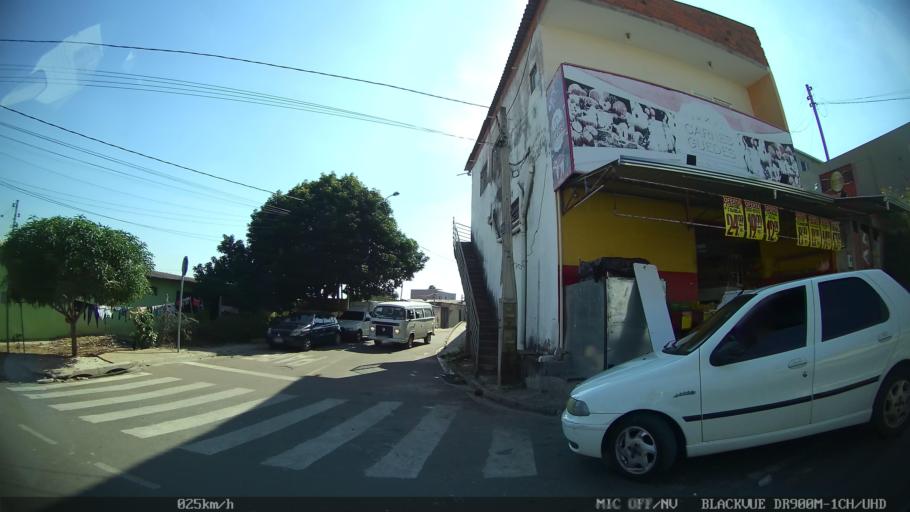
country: BR
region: Sao Paulo
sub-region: Campinas
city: Campinas
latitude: -22.9447
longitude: -47.0827
